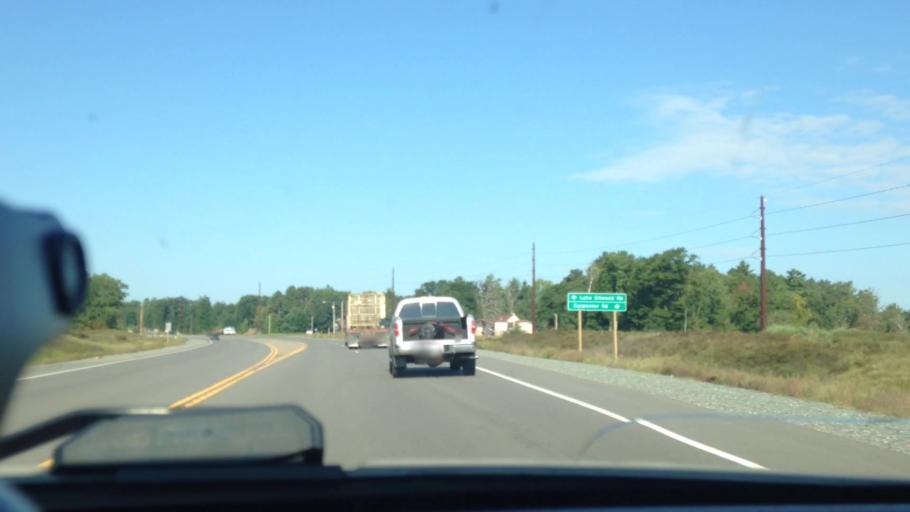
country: US
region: Michigan
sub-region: Dickinson County
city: Iron Mountain
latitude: 45.8810
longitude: -88.1262
